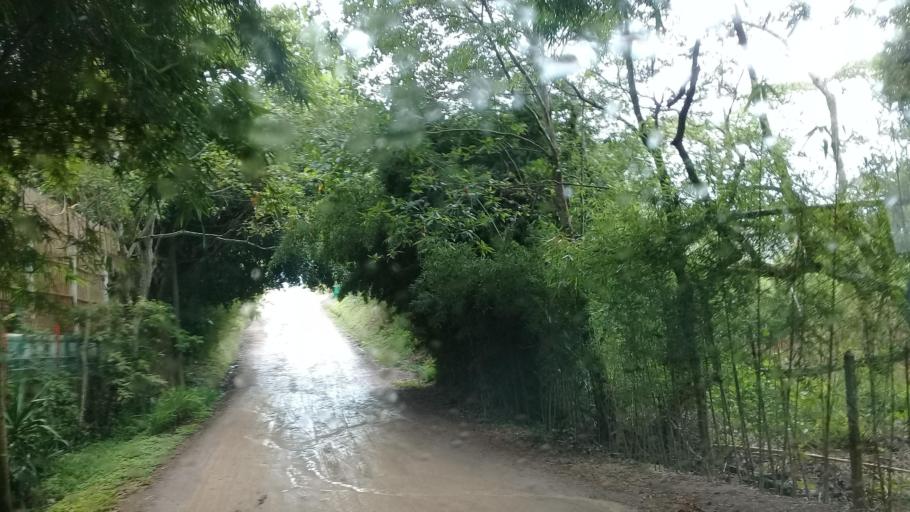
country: MX
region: Veracruz
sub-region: Emiliano Zapata
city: Jacarandas
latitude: 19.5057
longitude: -96.8436
